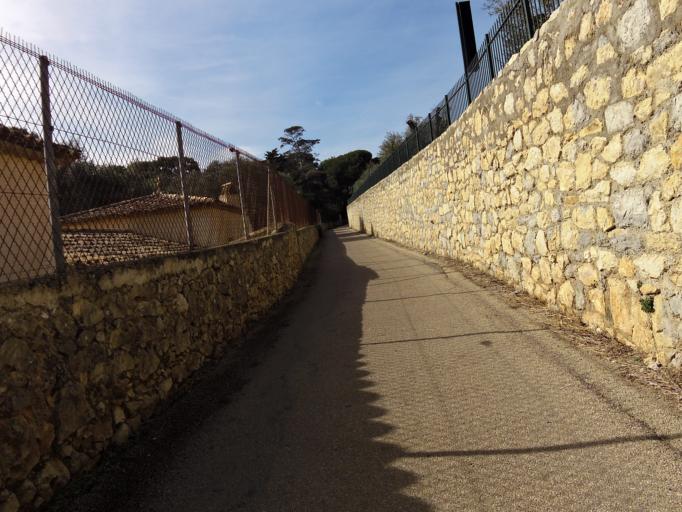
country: FR
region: Provence-Alpes-Cote d'Azur
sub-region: Departement des Alpes-Maritimes
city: Antibes
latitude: 43.5474
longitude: 7.1327
